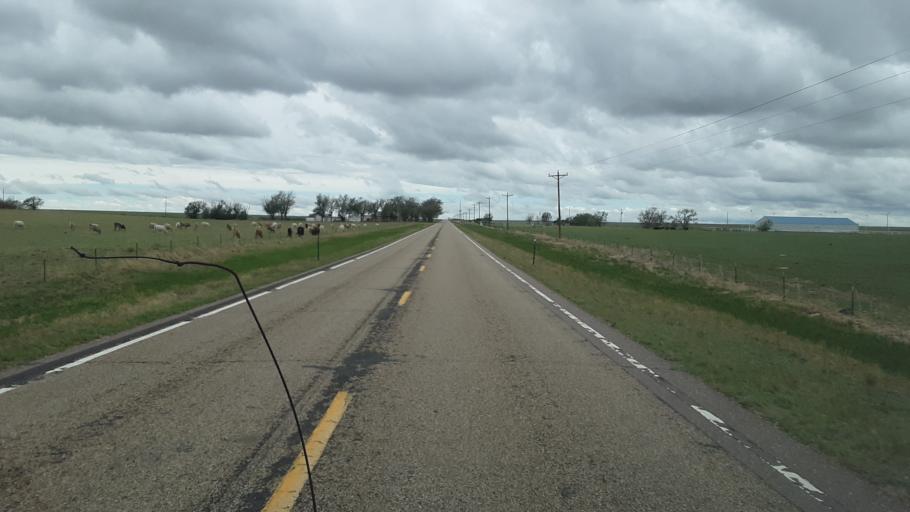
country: US
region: Colorado
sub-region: El Paso County
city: Ellicott
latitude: 38.8398
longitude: -103.9937
